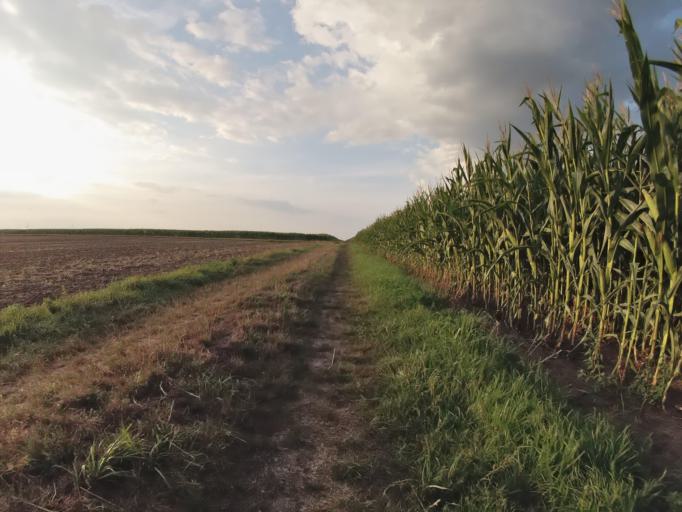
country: DE
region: North Rhine-Westphalia
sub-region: Regierungsbezirk Munster
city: Westerkappeln
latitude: 52.3457
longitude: 7.8888
